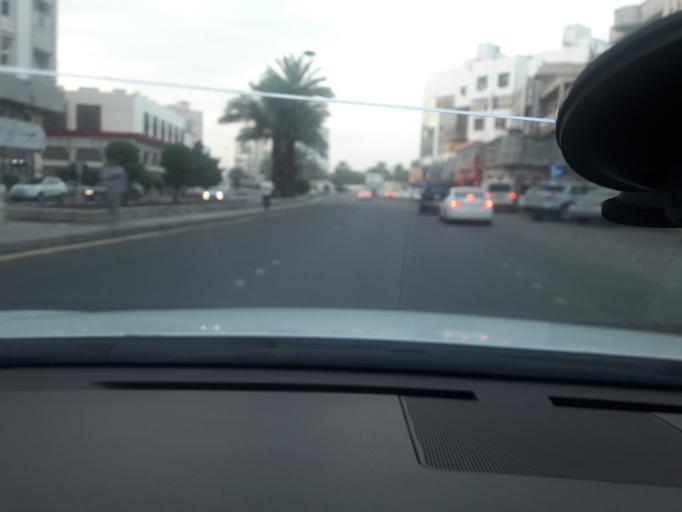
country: SA
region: Al Madinah al Munawwarah
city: Medina
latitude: 24.4797
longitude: 39.6022
